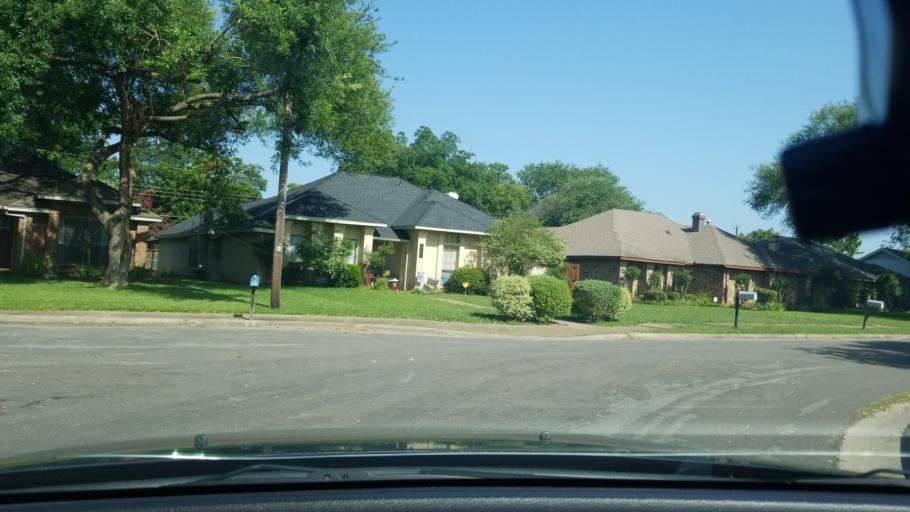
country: US
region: Texas
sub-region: Dallas County
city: Highland Park
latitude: 32.8097
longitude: -96.6927
